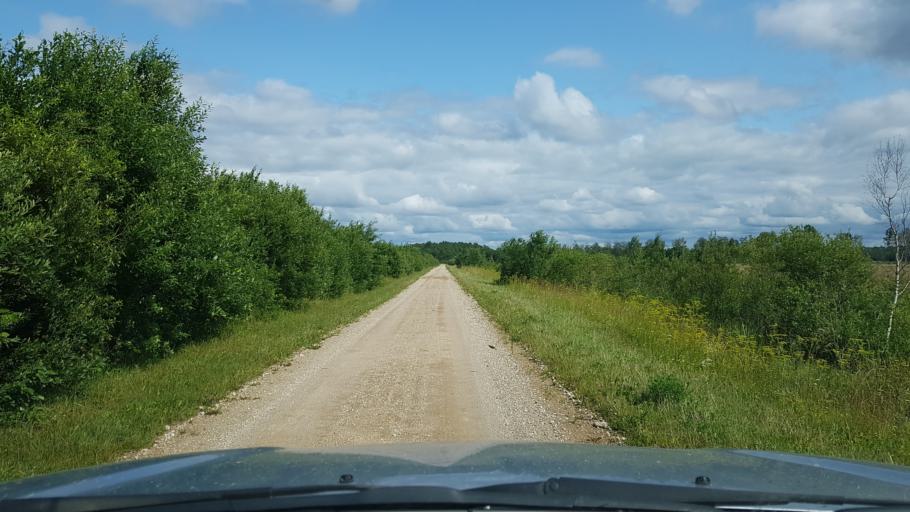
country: EE
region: Ida-Virumaa
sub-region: Sillamaee linn
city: Sillamae
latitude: 59.3703
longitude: 27.9146
